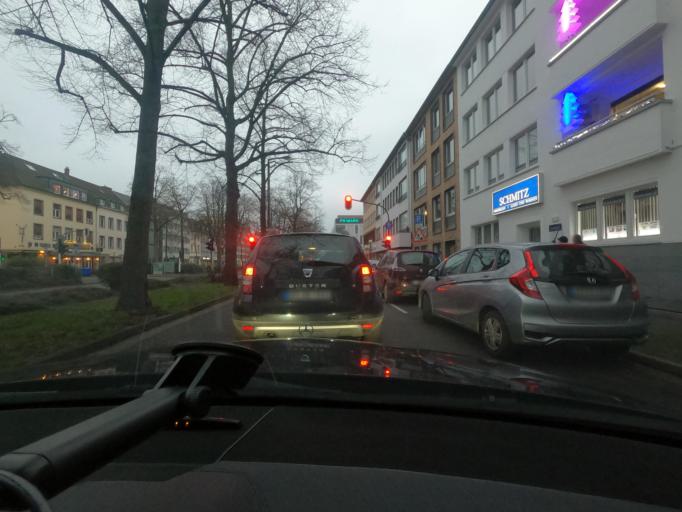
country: DE
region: North Rhine-Westphalia
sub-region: Regierungsbezirk Dusseldorf
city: Krefeld
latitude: 51.3356
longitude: 6.5645
